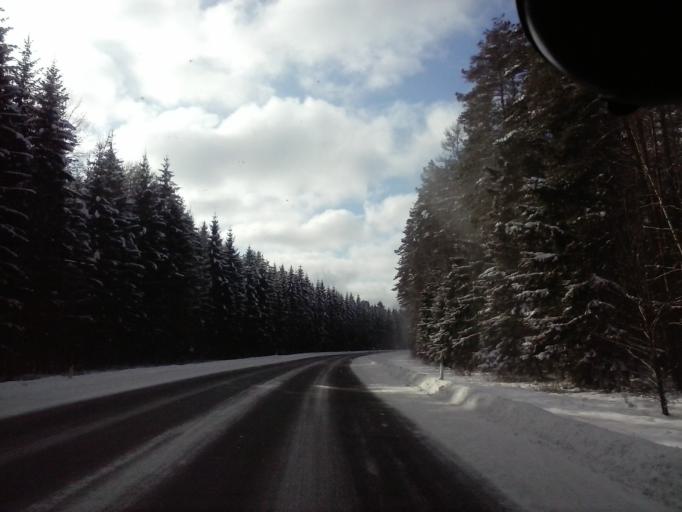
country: EE
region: Viljandimaa
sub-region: Moisakuela linn
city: Moisakula
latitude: 58.2239
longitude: 25.1054
